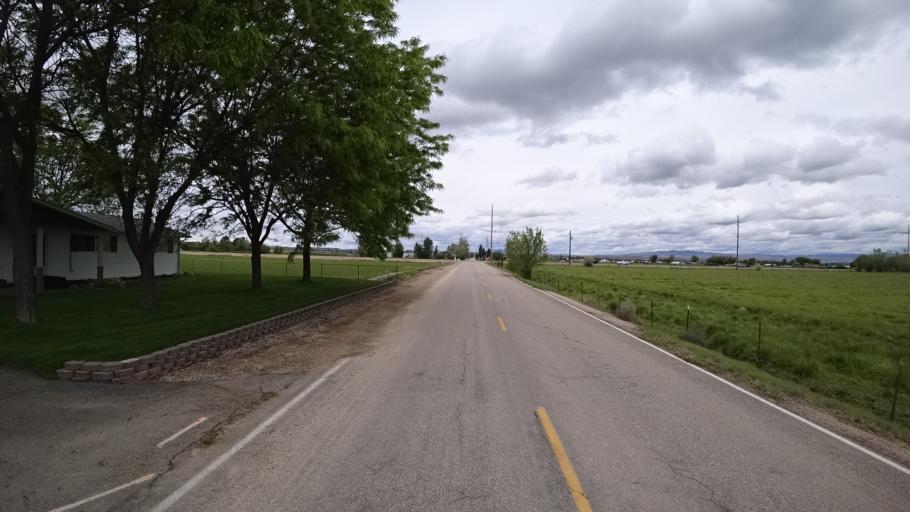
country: US
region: Idaho
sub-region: Ada County
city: Star
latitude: 43.6904
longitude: -116.4434
